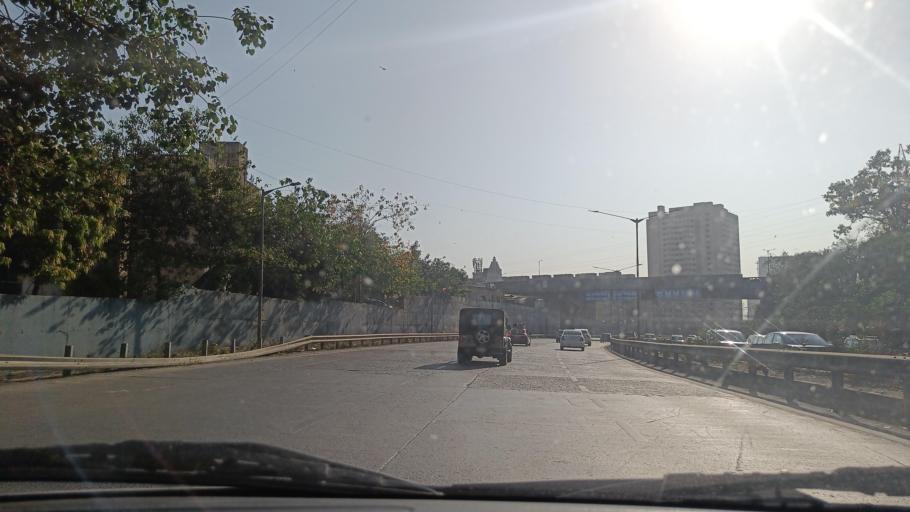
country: IN
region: Maharashtra
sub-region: Mumbai Suburban
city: Mumbai
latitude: 19.0337
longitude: 72.9030
